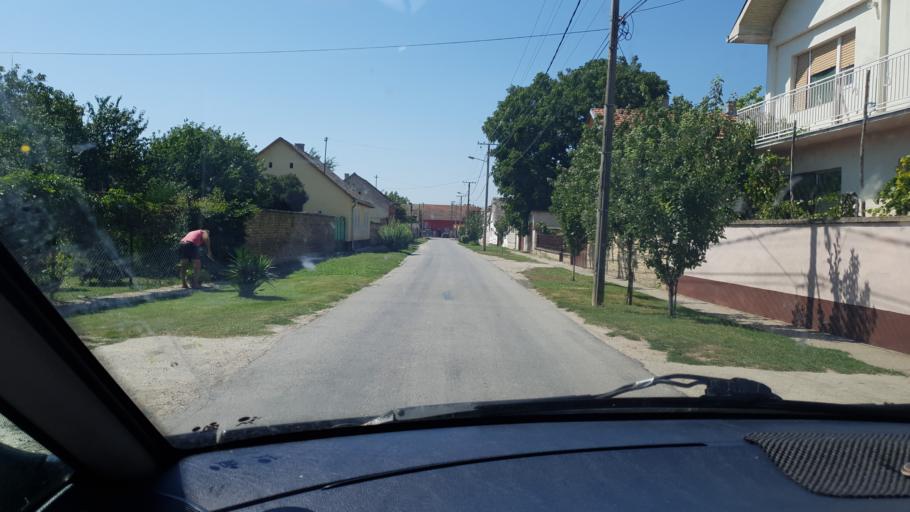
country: RS
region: Autonomna Pokrajina Vojvodina
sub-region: Juznobacki Okrug
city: Kovilj
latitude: 45.2258
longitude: 20.0235
